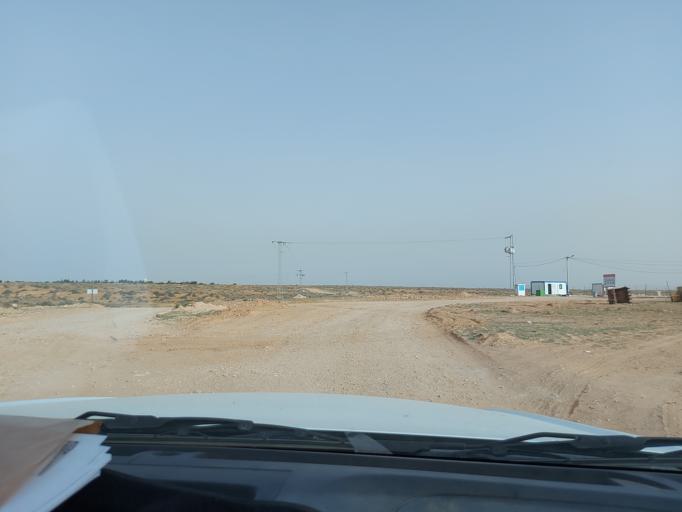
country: TN
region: Madanin
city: Medenine
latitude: 33.2664
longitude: 10.5699
